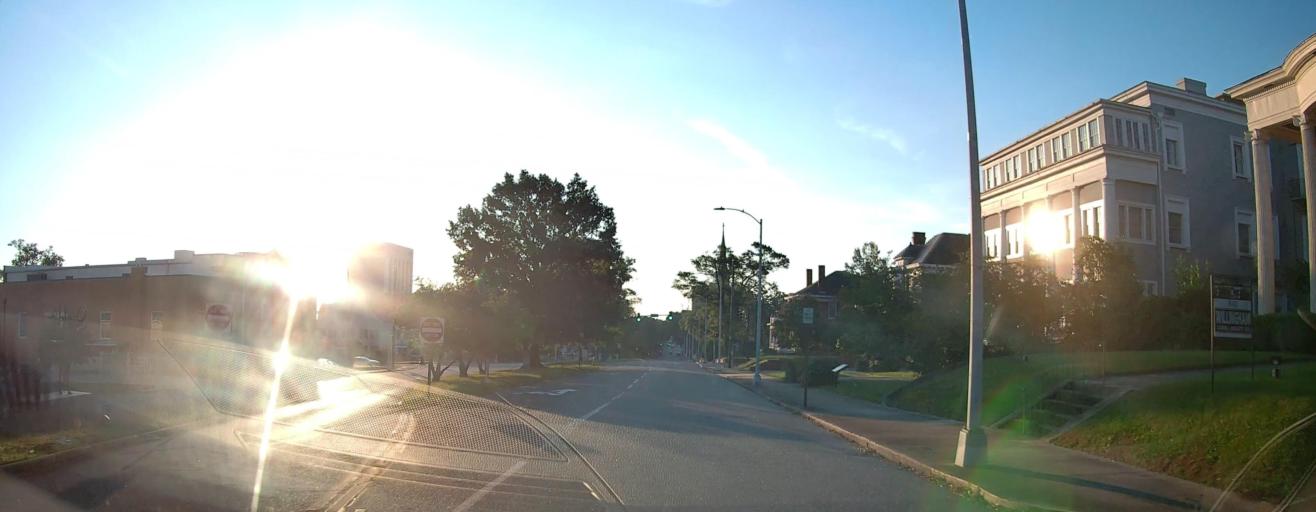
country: US
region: Georgia
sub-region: Bibb County
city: Macon
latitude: 32.8401
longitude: -83.6318
